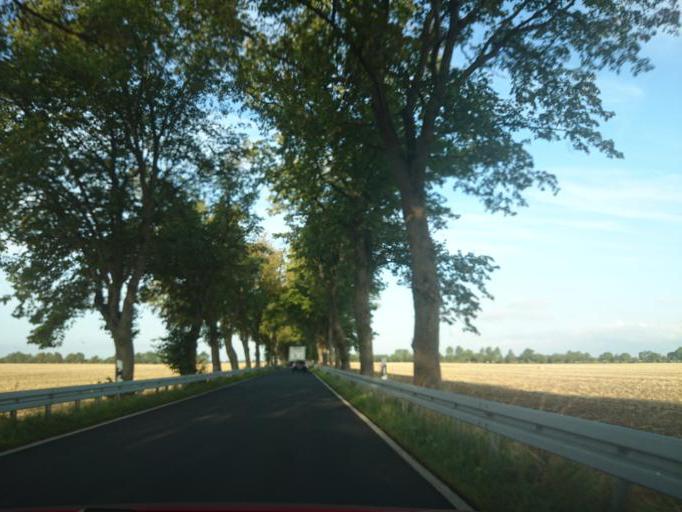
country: DE
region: Mecklenburg-Vorpommern
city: Niepars
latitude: 54.3338
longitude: 12.8742
